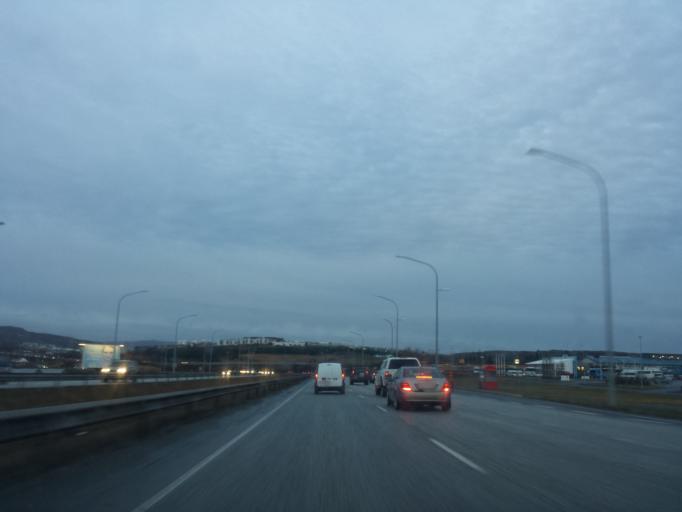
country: IS
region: Capital Region
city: Reykjavik
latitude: 64.1243
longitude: -21.7967
